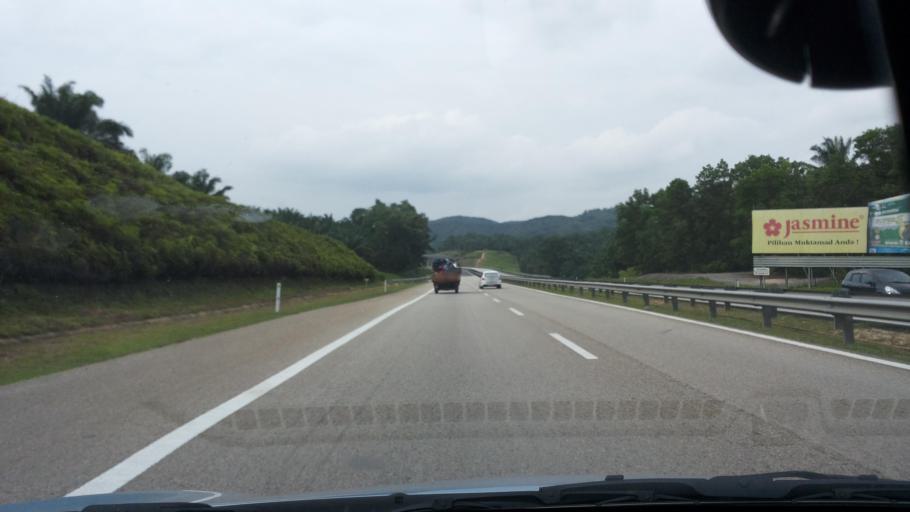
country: MY
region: Pahang
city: Kuantan
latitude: 3.7970
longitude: 103.1598
